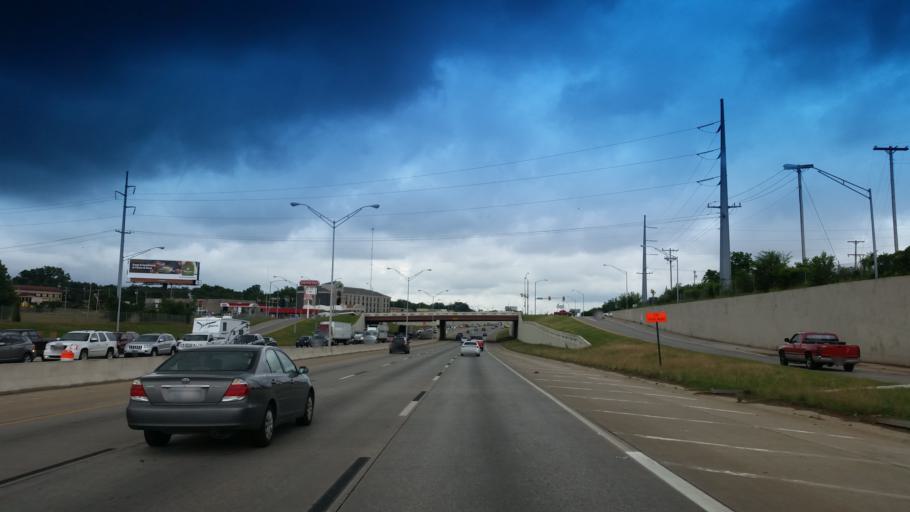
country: US
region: Oklahoma
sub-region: Oklahoma County
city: Oklahoma City
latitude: 35.4519
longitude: -97.4886
